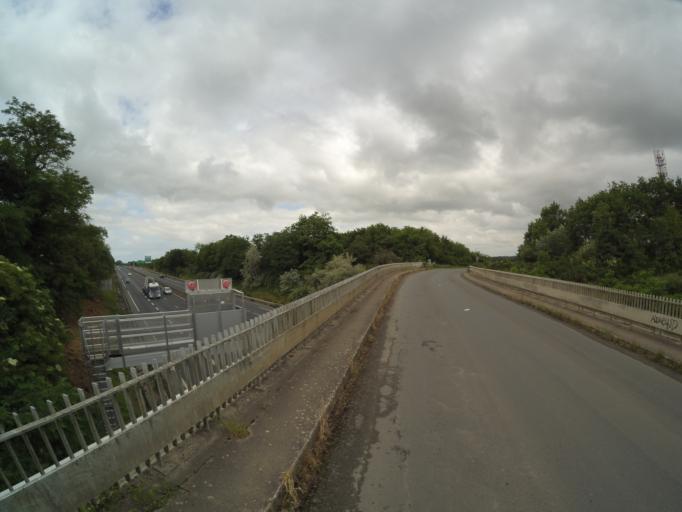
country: FR
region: Poitou-Charentes
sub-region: Departement de la Charente-Maritime
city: Breuil-Magne
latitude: 45.9647
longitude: -0.9703
